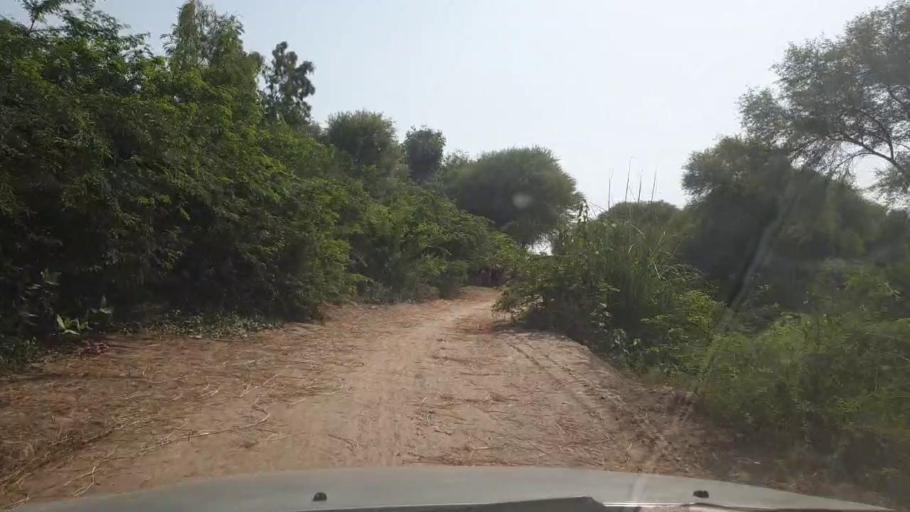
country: PK
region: Sindh
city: Bulri
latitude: 24.8718
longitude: 68.3106
